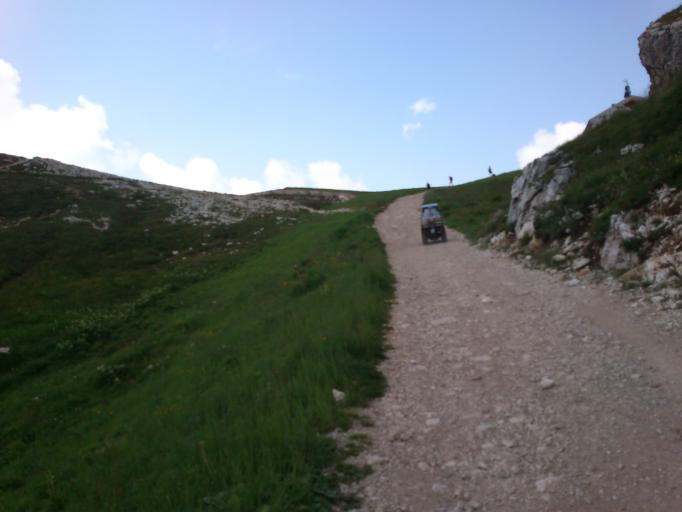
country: IT
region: Veneto
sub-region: Provincia di Belluno
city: Selva di Cadore
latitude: 46.5006
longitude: 12.0414
